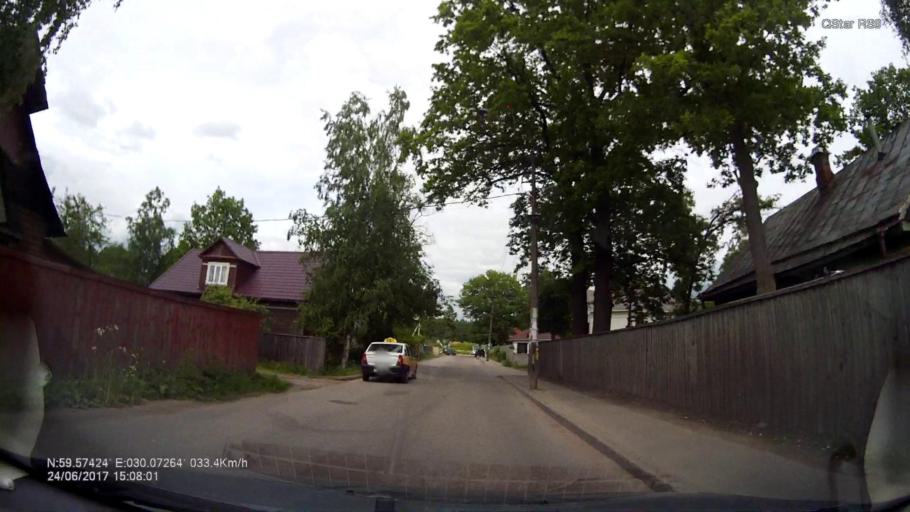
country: RU
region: Leningrad
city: Mariyenburg
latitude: 59.5743
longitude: 30.0727
